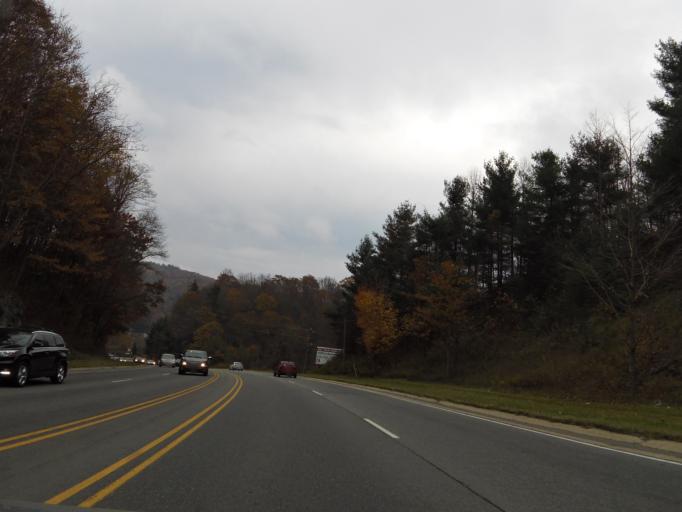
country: US
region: North Carolina
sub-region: Watauga County
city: Boone
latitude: 36.1825
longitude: -81.6503
